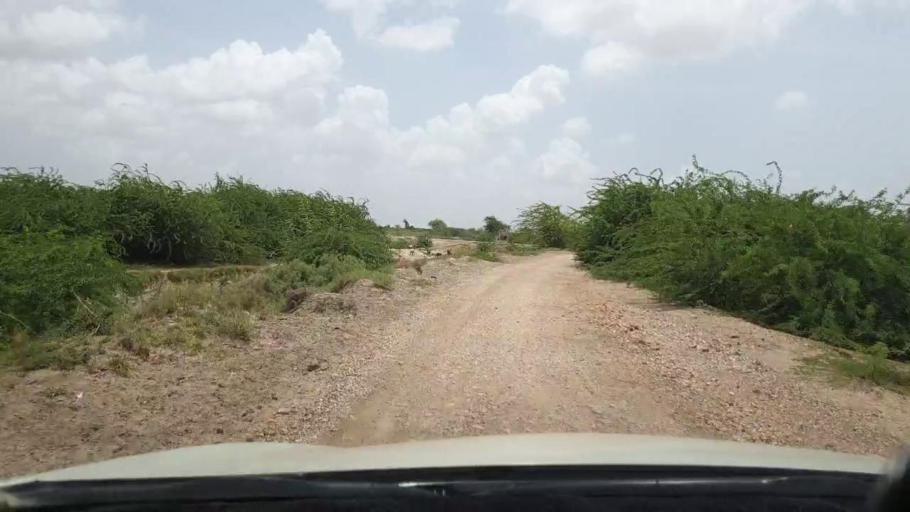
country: PK
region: Sindh
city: Kadhan
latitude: 24.3614
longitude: 68.9266
